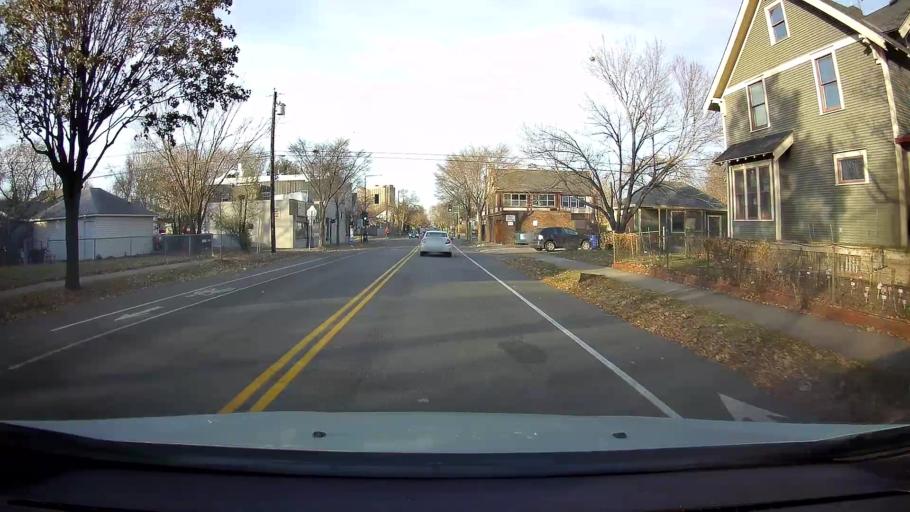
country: US
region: Minnesota
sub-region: Ramsey County
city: Falcon Heights
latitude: 44.9585
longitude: -93.1568
